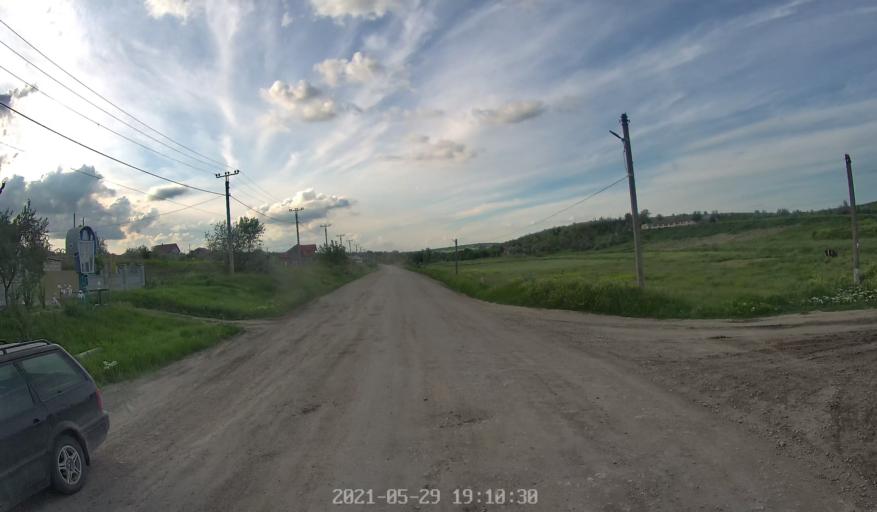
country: MD
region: Chisinau
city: Singera
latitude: 46.8334
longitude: 28.9560
